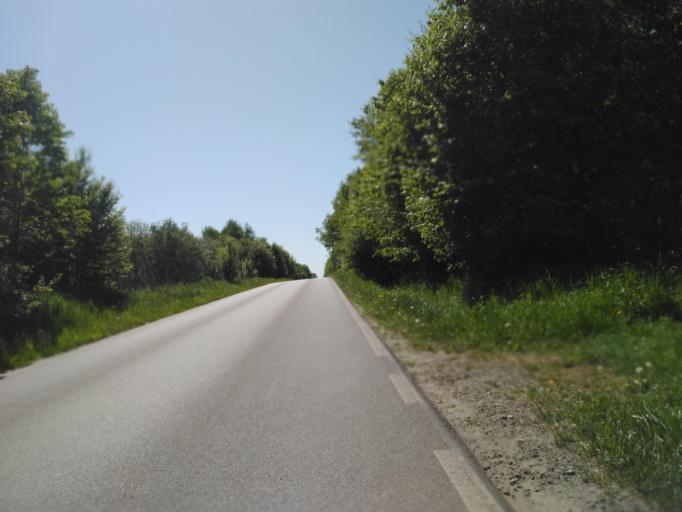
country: PL
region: Subcarpathian Voivodeship
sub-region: Krosno
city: Krosno
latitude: 49.6739
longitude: 21.7877
